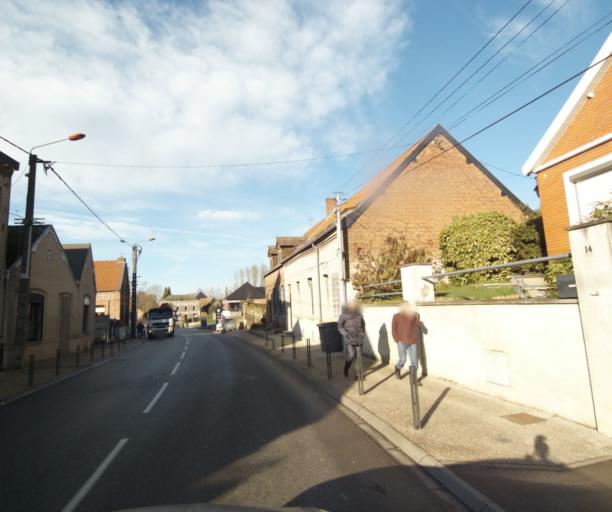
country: FR
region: Nord-Pas-de-Calais
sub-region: Departement du Nord
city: Preseau
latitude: 50.3136
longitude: 3.5752
